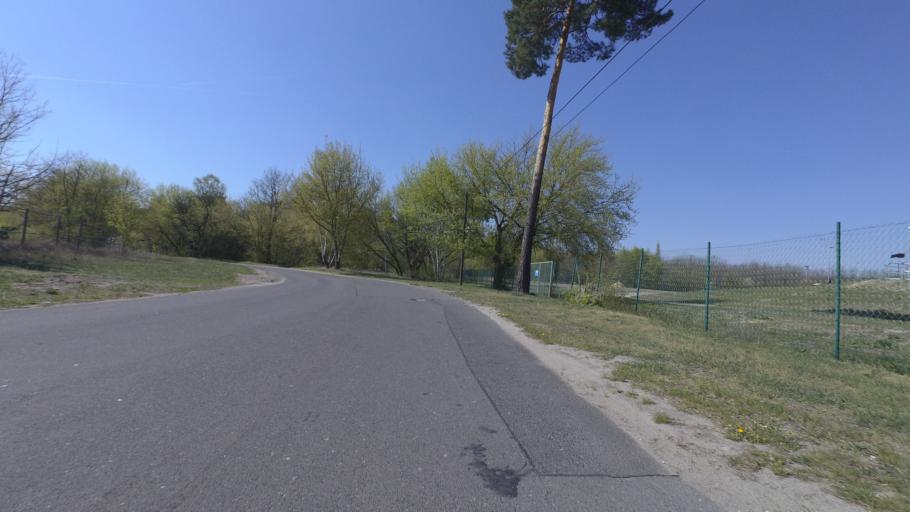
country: DE
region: Brandenburg
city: Zossen
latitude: 52.1715
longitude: 13.4802
